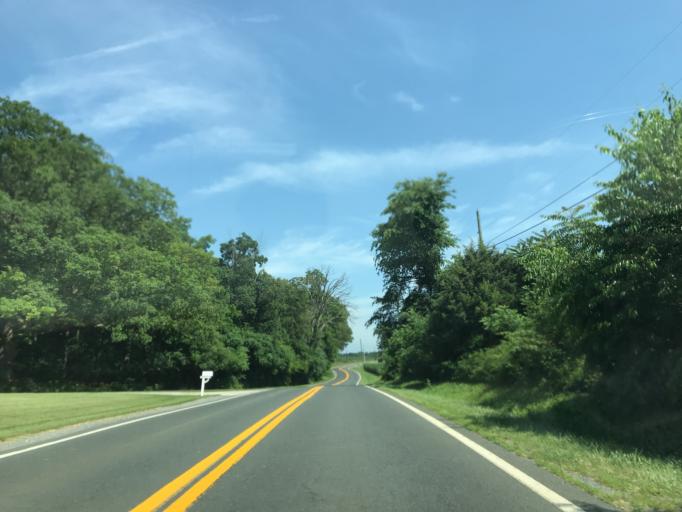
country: US
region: Maryland
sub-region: Carroll County
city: Taneytown
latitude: 39.6101
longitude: -77.1287
